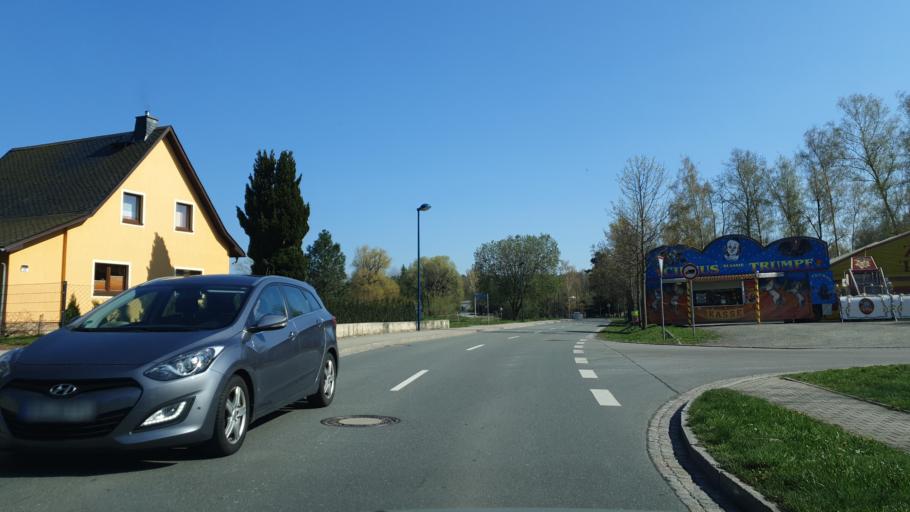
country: DE
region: Saxony
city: Oelsnitz
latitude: 50.7212
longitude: 12.7020
